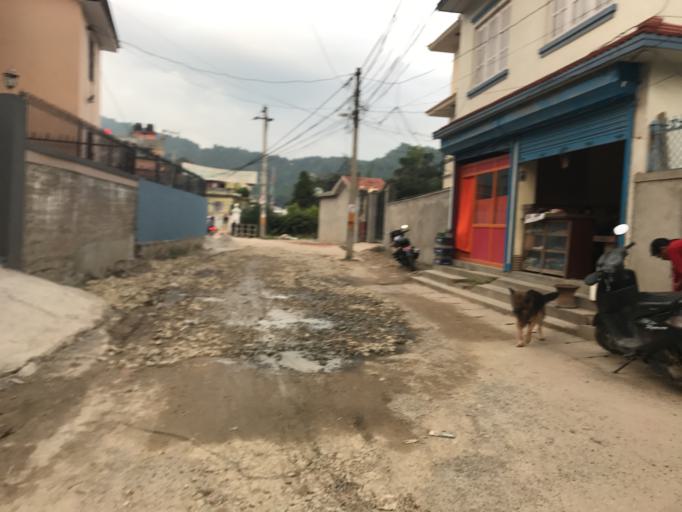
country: NP
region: Central Region
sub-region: Bagmati Zone
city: Kathmandu
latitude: 27.7744
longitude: 85.3621
